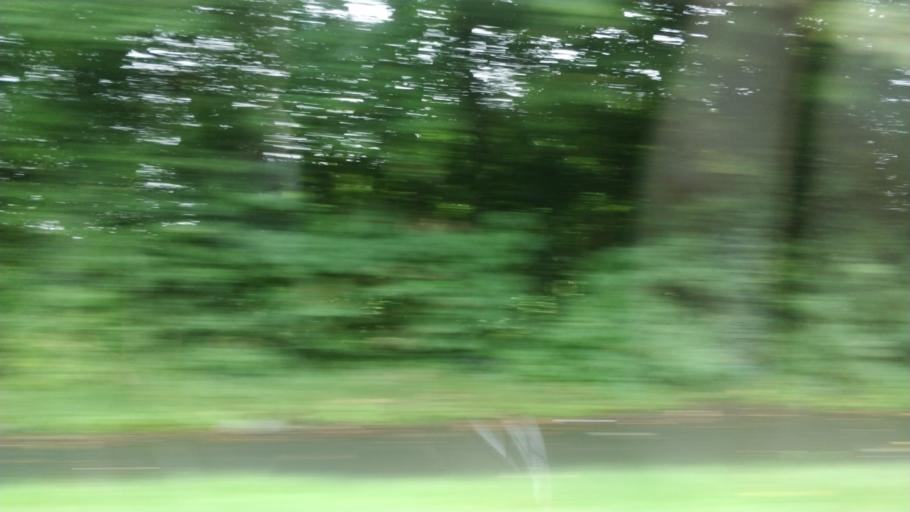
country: GB
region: England
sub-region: Sefton
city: Maghull
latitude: 53.5151
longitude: -2.9418
